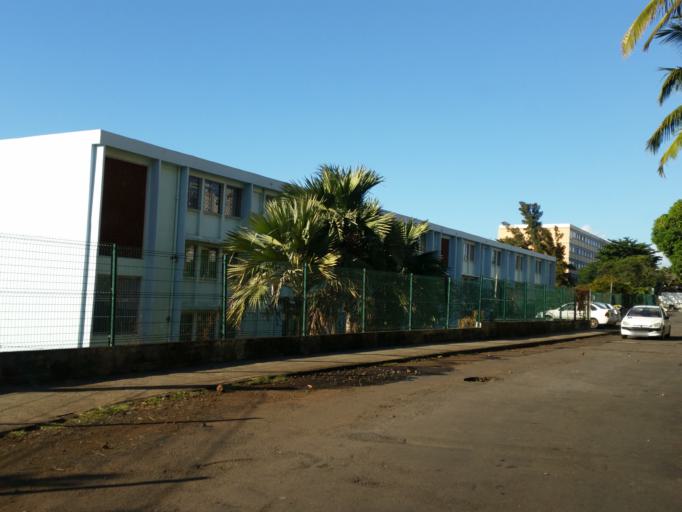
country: RE
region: Reunion
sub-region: Reunion
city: Saint-Denis
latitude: -20.8989
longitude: 55.4616
